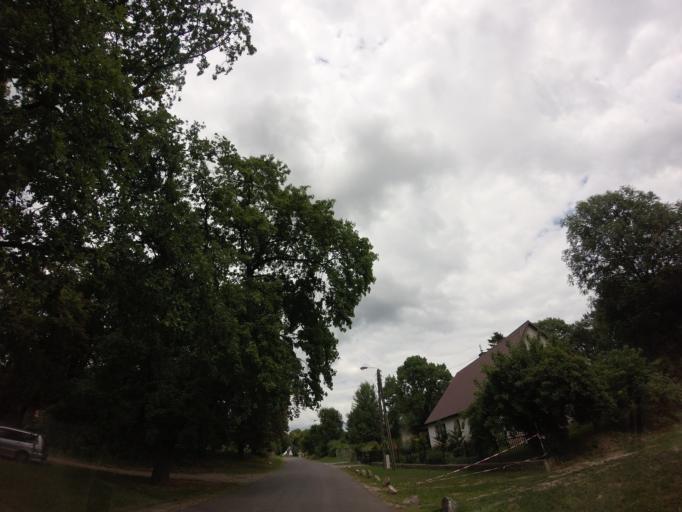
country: PL
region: West Pomeranian Voivodeship
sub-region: Powiat choszczenski
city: Choszczno
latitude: 53.1669
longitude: 15.4982
